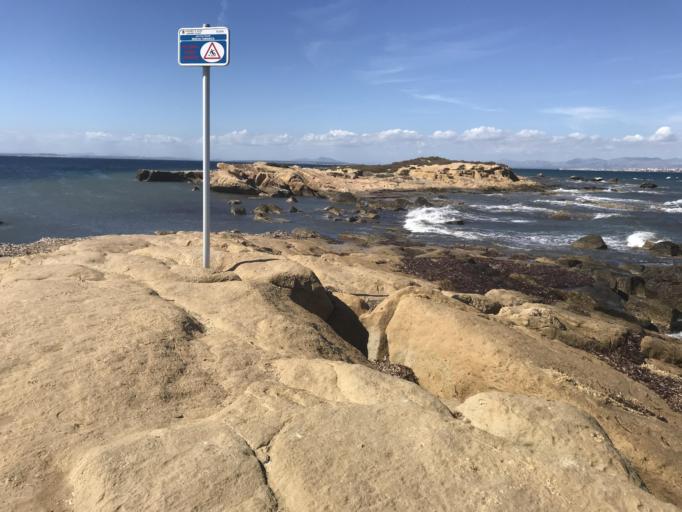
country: ES
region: Valencia
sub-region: Provincia de Alicante
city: Santa Pola
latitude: 38.1668
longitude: -0.4848
